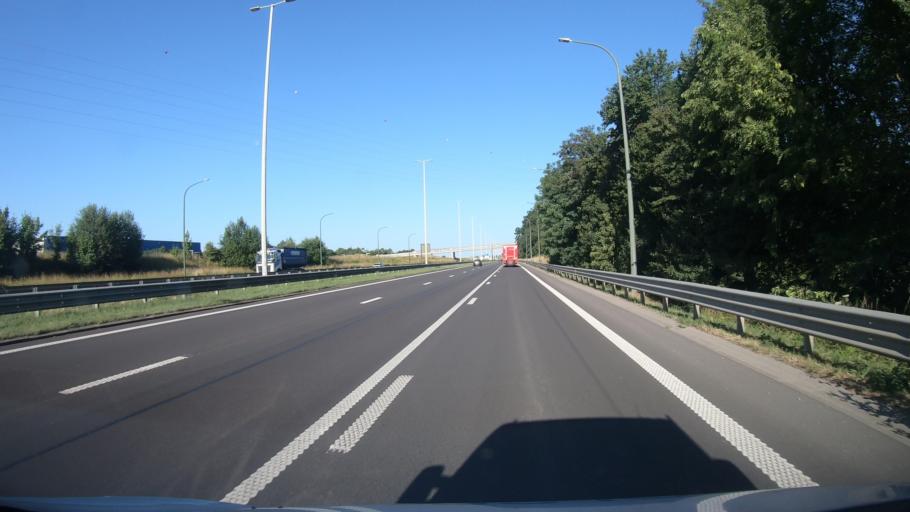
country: BE
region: Wallonia
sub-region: Province de Liege
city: Dison
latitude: 50.6441
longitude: 5.8872
